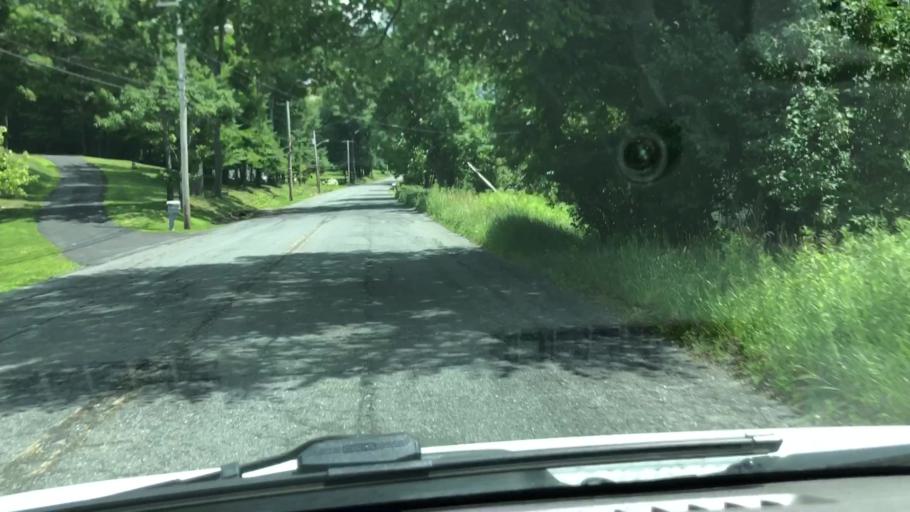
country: US
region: Massachusetts
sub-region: Berkshire County
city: Adams
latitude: 42.5862
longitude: -73.1046
